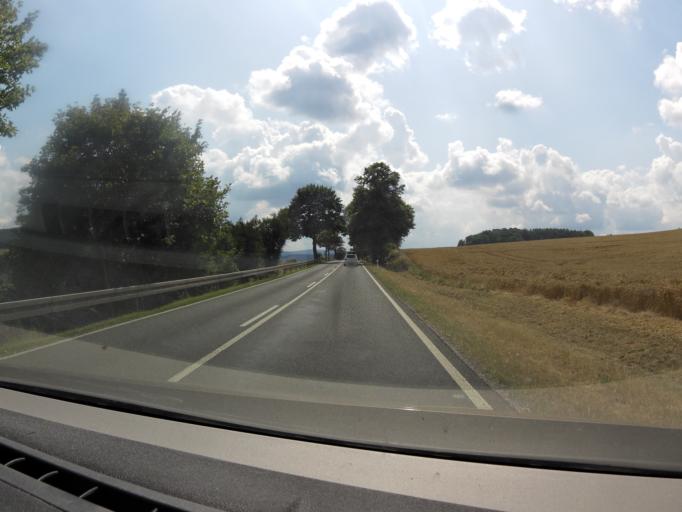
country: DE
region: Thuringia
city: Plaue
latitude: 50.7844
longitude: 10.9035
